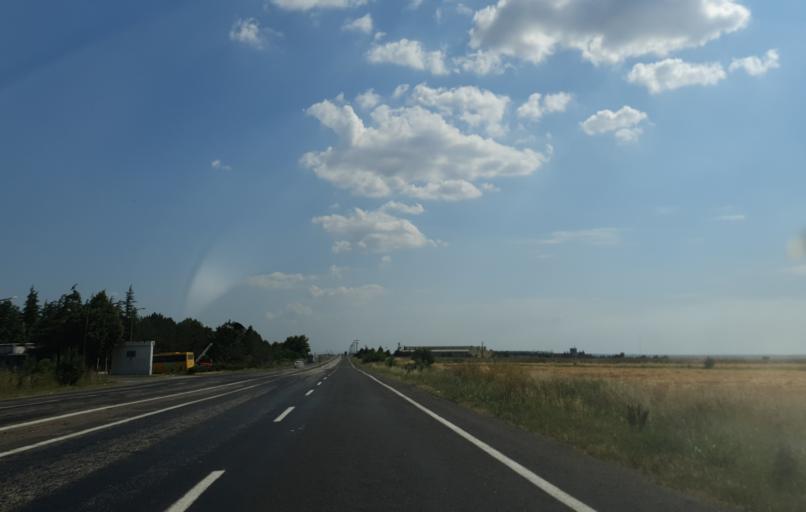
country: TR
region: Kirklareli
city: Buyukkaristiran
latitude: 41.2767
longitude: 27.5548
